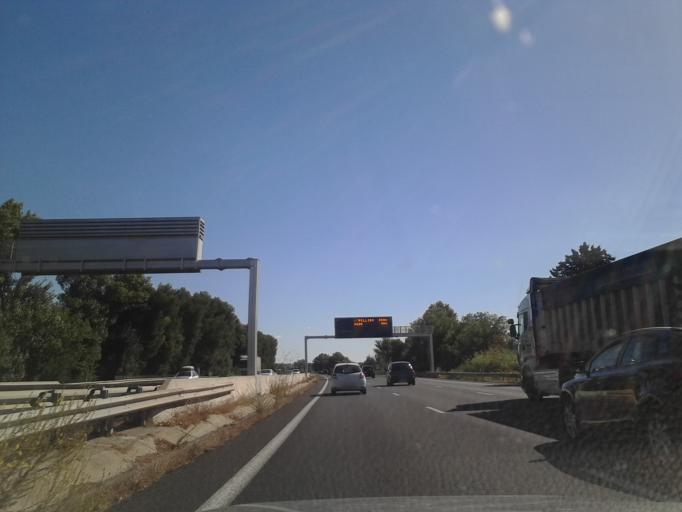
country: FR
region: Languedoc-Roussillon
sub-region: Departement de l'Herault
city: Sauvian
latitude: 43.3102
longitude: 3.2500
